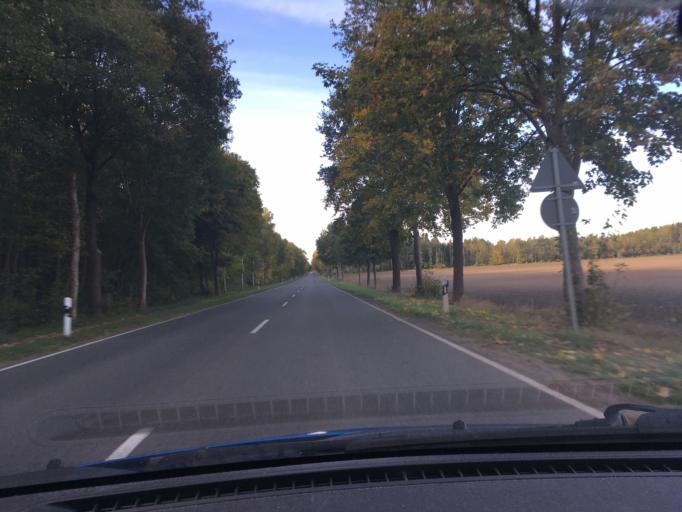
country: DE
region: Lower Saxony
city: Fassberg
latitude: 52.9358
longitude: 10.1338
